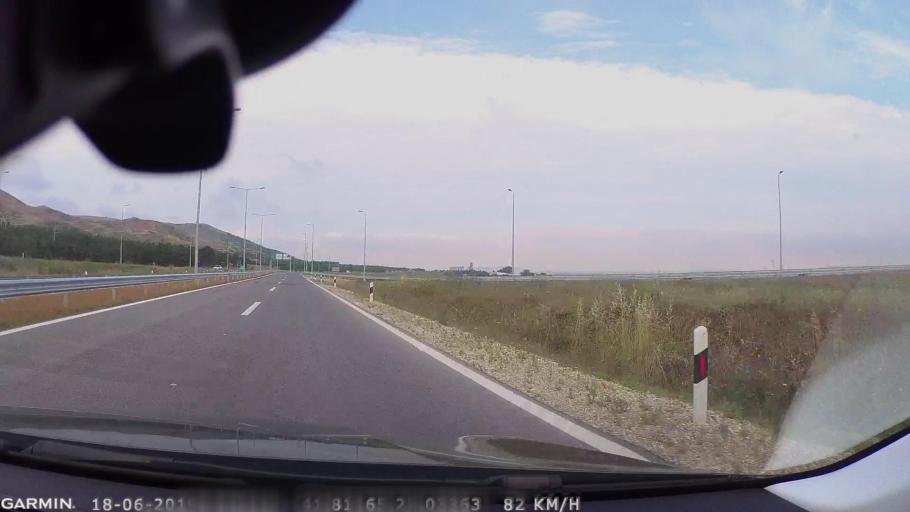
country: MK
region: Sveti Nikole
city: Sveti Nikole
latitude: 41.8110
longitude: 22.0328
